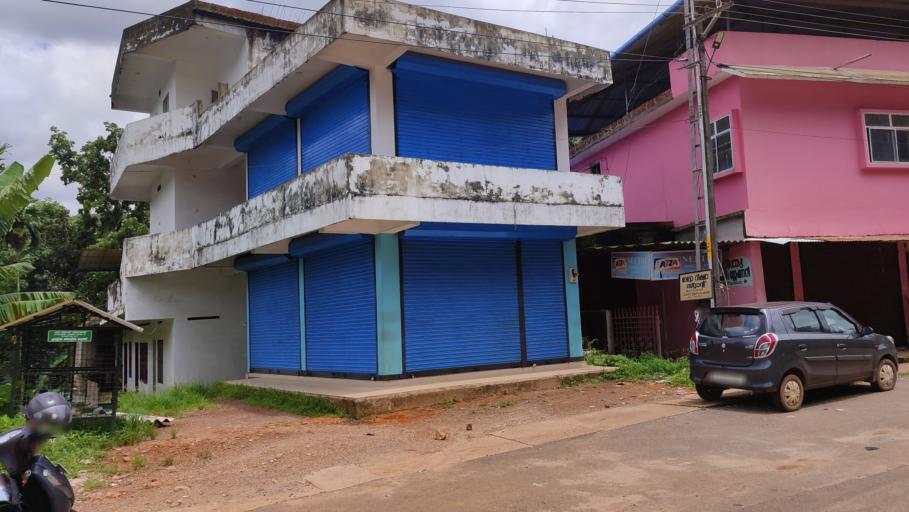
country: IN
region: Kerala
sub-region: Kasaragod District
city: Nileshwar
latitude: 12.2964
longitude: 75.2813
